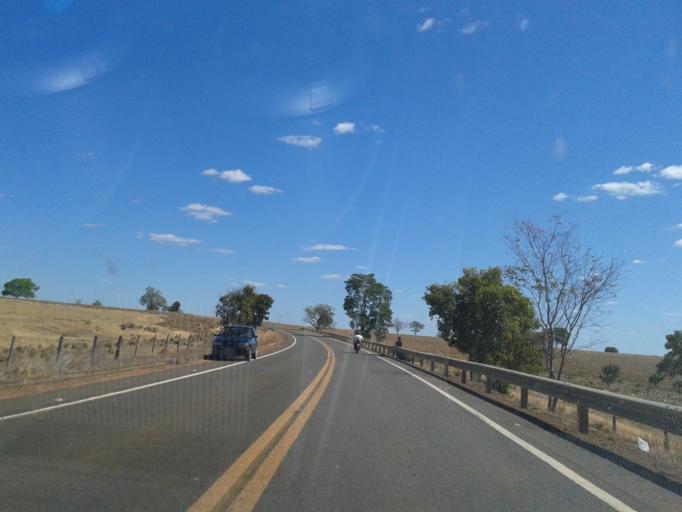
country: BR
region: Goias
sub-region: Sao Miguel Do Araguaia
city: Sao Miguel do Araguaia
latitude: -13.4008
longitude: -50.2577
